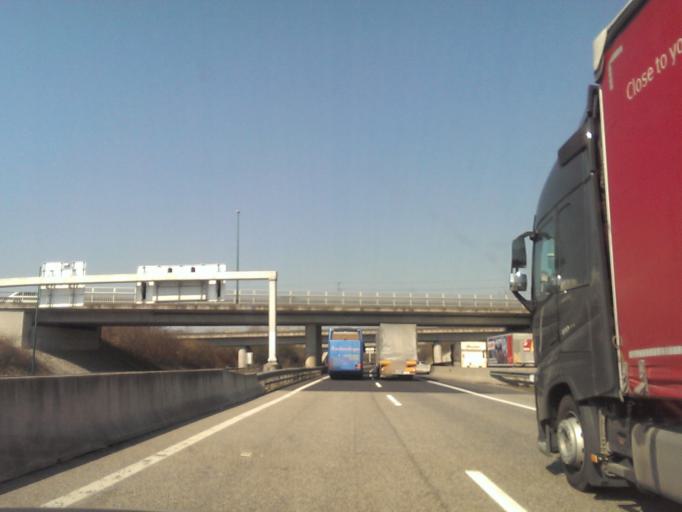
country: AT
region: Upper Austria
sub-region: Wels-Land
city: Gunskirchen
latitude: 48.1509
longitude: 13.9819
